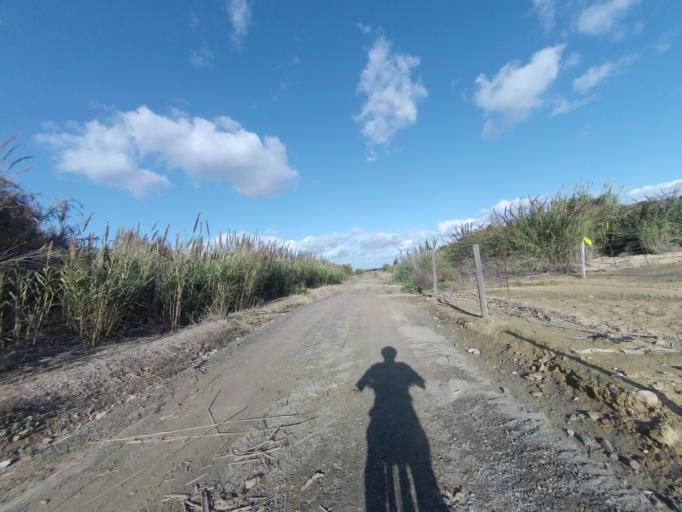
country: ES
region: Andalusia
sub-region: Provincia de Huelva
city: Palos de la Frontera
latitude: 37.2573
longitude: -6.8752
